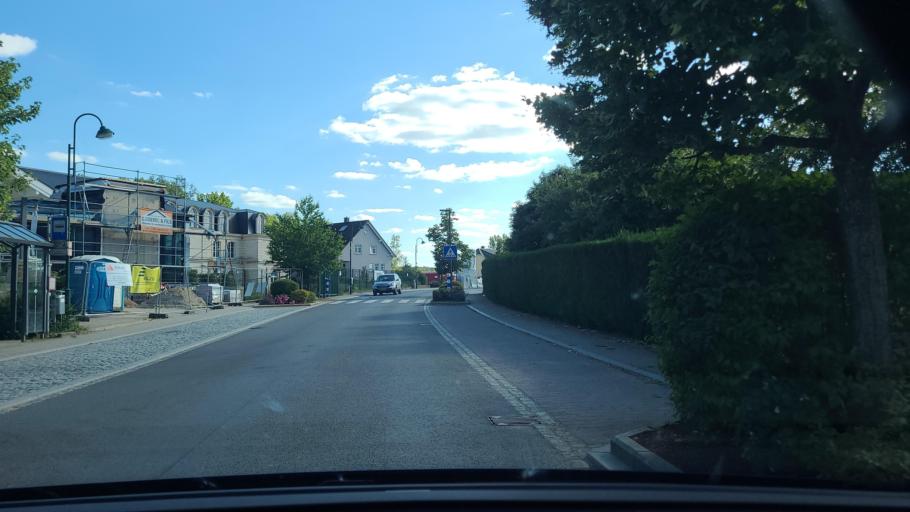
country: LU
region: Luxembourg
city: Capellen
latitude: 49.6160
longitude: 5.9932
